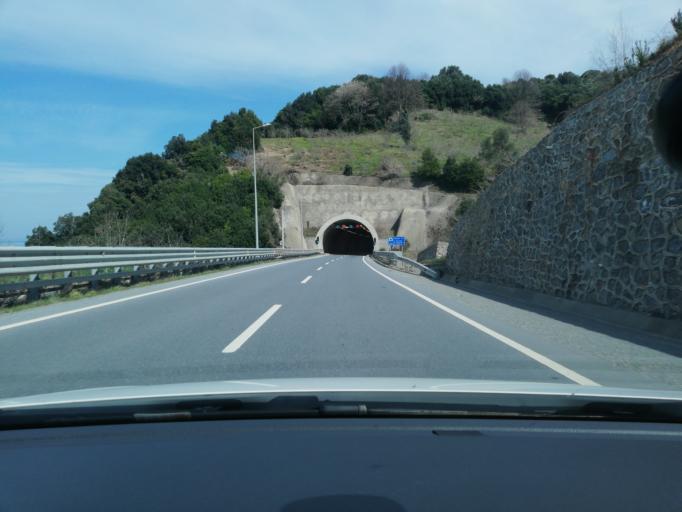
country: TR
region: Zonguldak
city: Alapli
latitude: 41.1642
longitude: 31.3621
